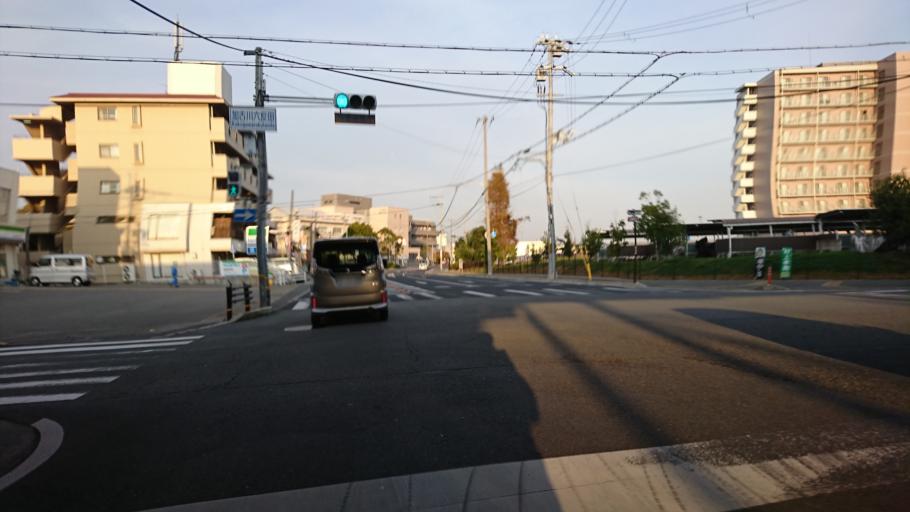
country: JP
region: Hyogo
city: Kakogawacho-honmachi
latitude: 34.7496
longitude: 134.8683
